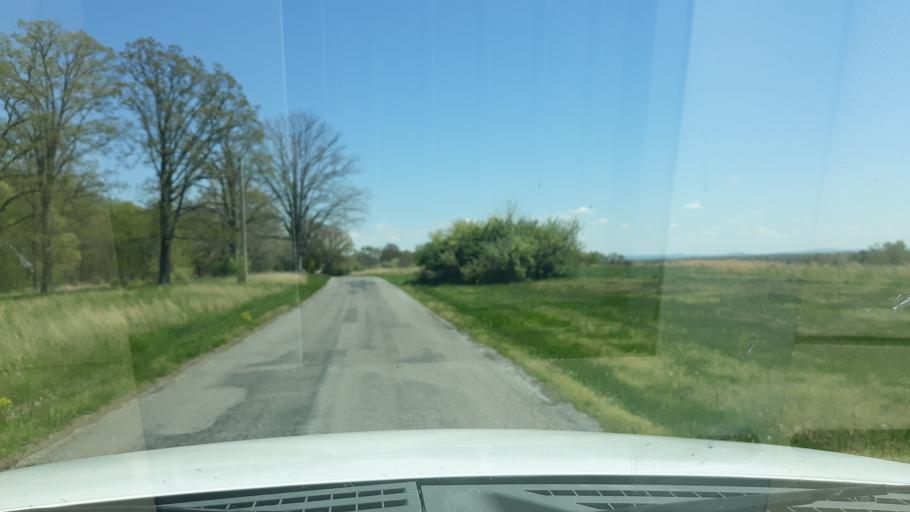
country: US
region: Illinois
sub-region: Saline County
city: Harrisburg
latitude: 37.8565
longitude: -88.6370
